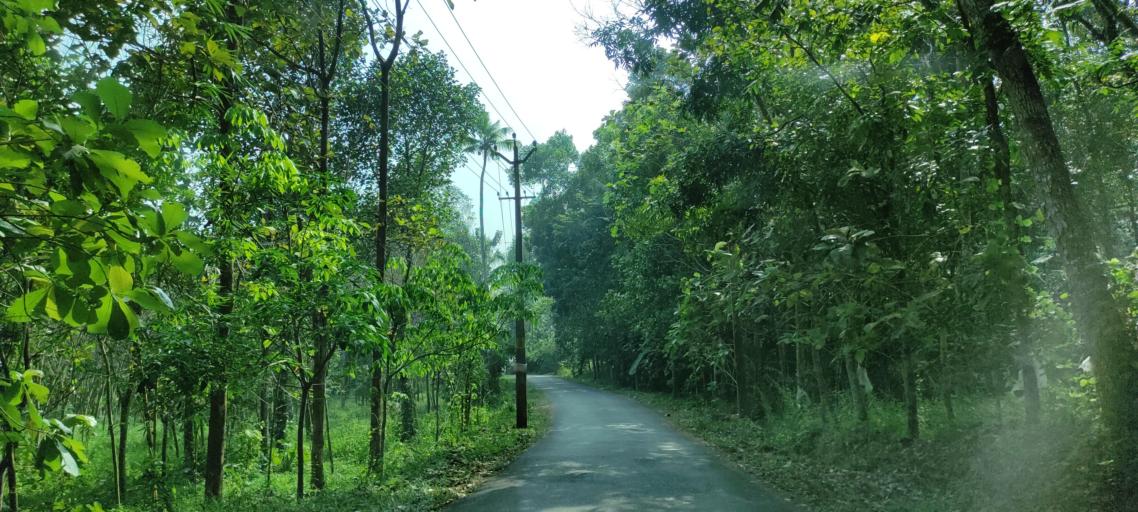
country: IN
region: Kerala
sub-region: Ernakulam
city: Piravam
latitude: 9.8055
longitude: 76.5257
